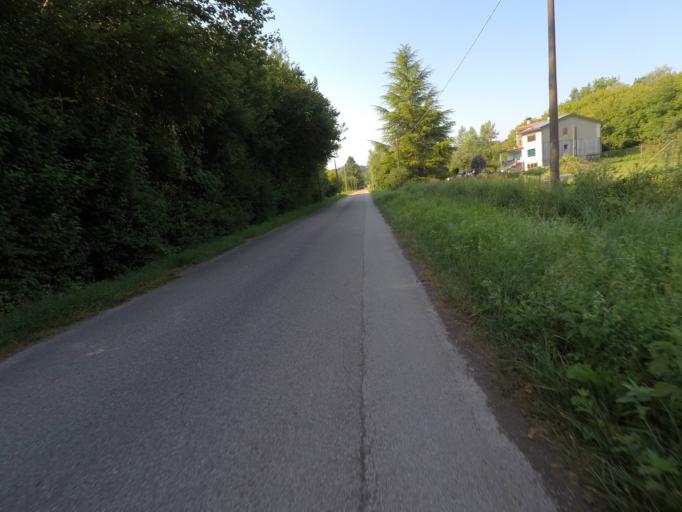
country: IT
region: Friuli Venezia Giulia
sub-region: Provincia di Pordenone
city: Pinzano al Tagliamento
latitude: 46.1980
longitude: 12.9571
